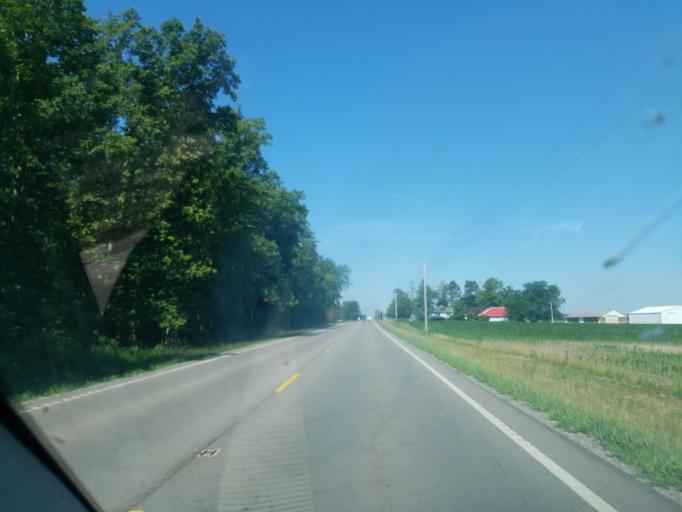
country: US
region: Ohio
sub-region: Logan County
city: Lakeview
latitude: 40.4390
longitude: -83.9491
